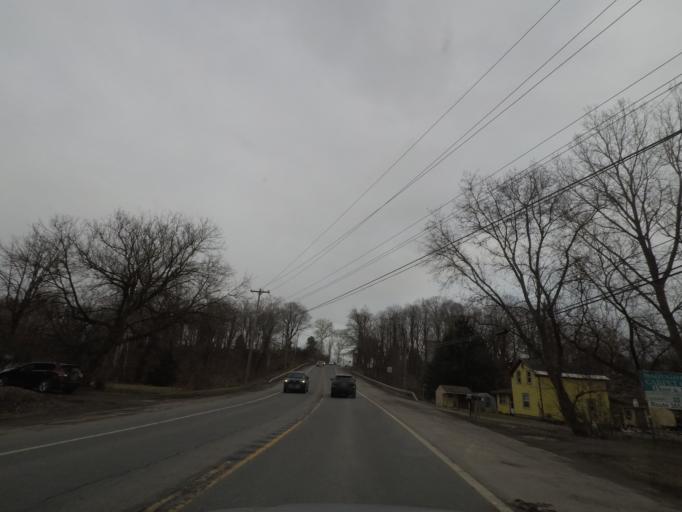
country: US
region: New York
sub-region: Madison County
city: Wampsville
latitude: 43.0758
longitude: -75.6974
